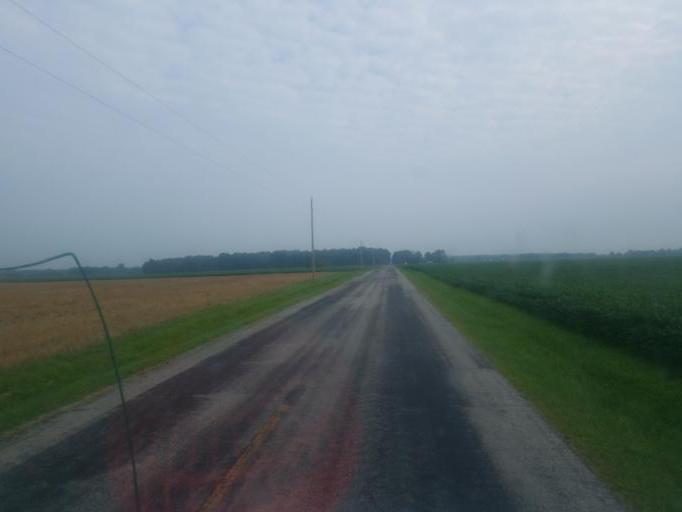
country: US
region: Ohio
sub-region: Morrow County
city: Cardington
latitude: 40.5712
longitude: -82.9766
